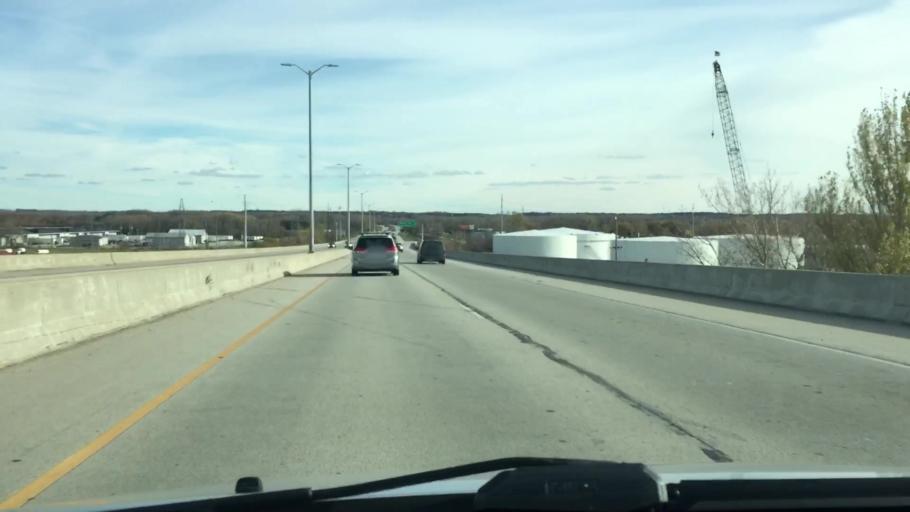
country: US
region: Wisconsin
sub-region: Brown County
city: Green Bay
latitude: 44.5301
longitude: -87.9976
